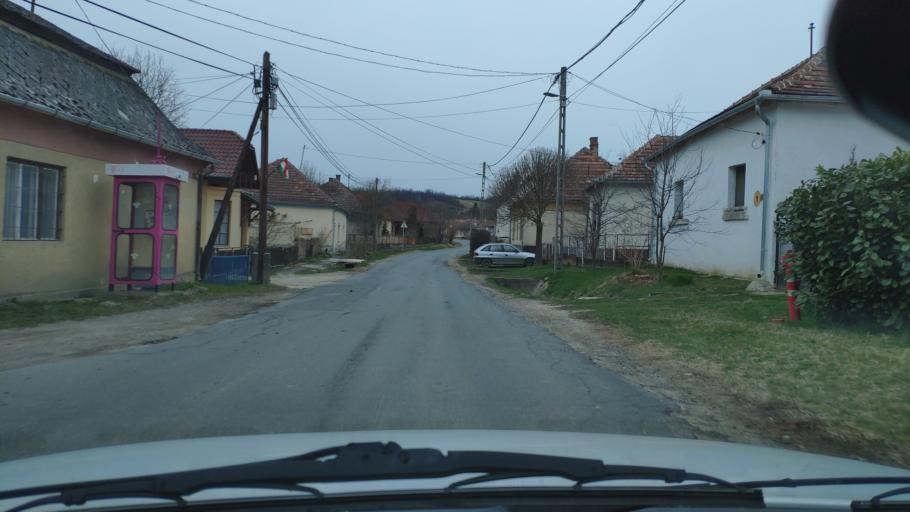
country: HU
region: Zala
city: Pacsa
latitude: 46.6745
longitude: 17.0557
